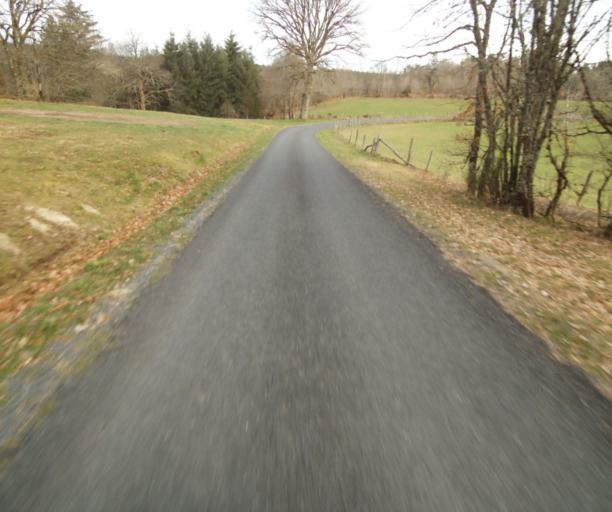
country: FR
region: Limousin
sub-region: Departement de la Correze
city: Treignac
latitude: 45.4524
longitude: 1.8092
